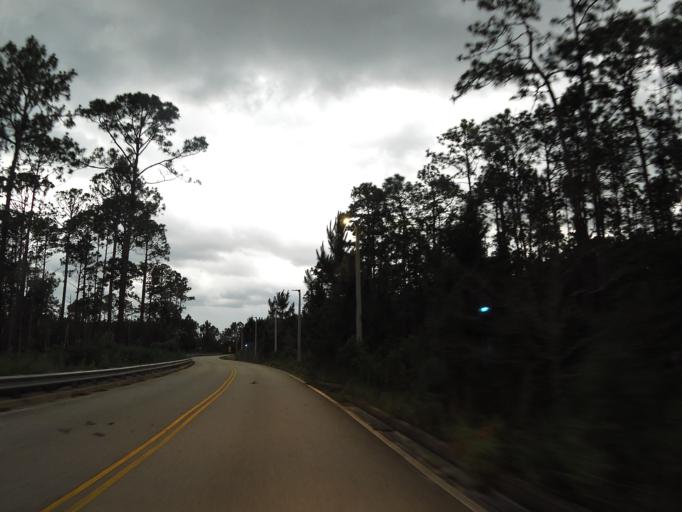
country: US
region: Florida
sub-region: Duval County
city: Jacksonville Beach
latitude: 30.2740
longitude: -81.5139
